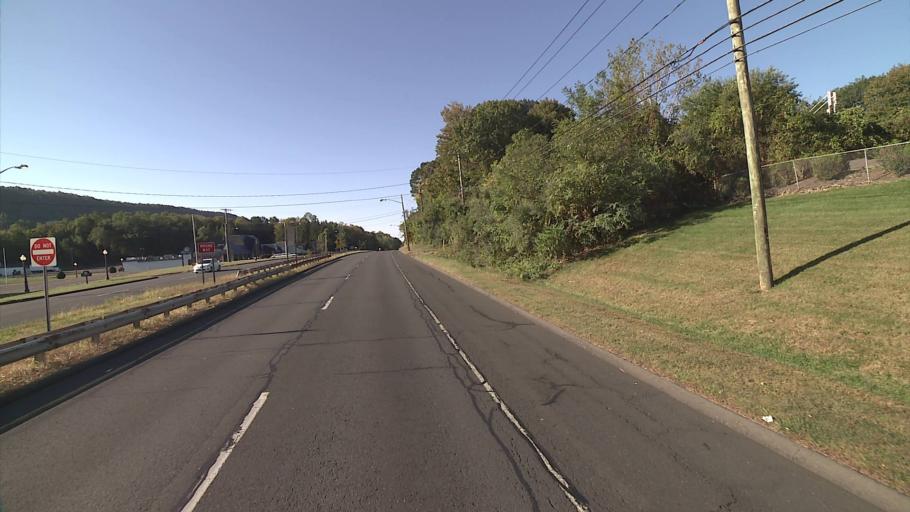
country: US
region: Connecticut
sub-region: Hartford County
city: Kensington
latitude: 41.5888
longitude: -72.7602
